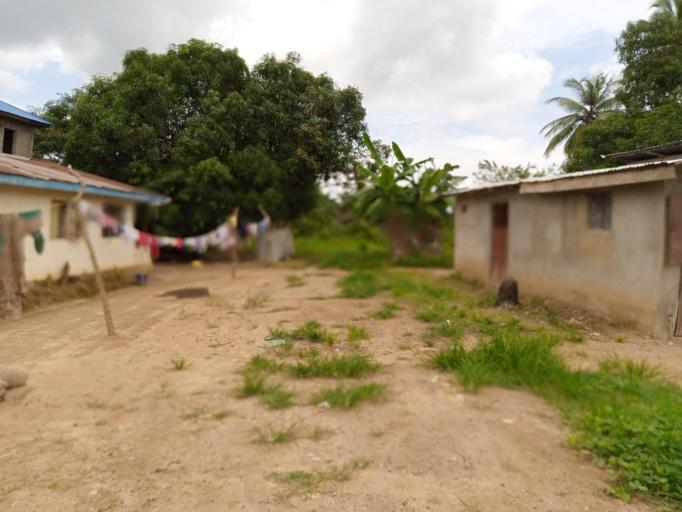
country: SL
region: Northern Province
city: Masoyila
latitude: 8.5578
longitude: -13.1643
